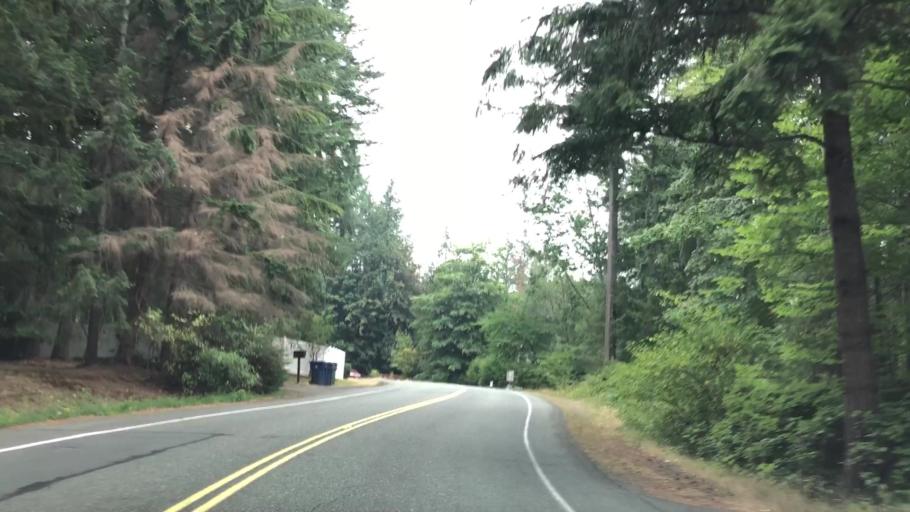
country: US
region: Washington
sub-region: King County
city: Cottage Lake
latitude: 47.7473
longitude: -122.1115
